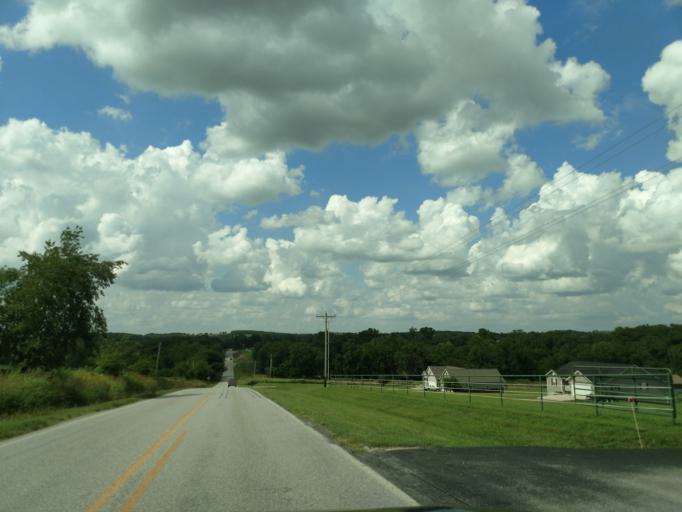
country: US
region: Arkansas
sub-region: Carroll County
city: Berryville
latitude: 36.3974
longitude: -93.5660
